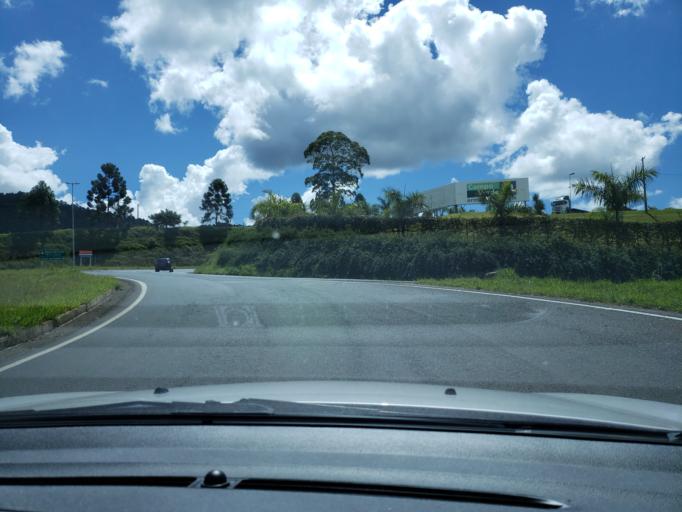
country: BR
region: Minas Gerais
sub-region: Pocos De Caldas
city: Pocos de Caldas
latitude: -21.8423
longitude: -46.6768
